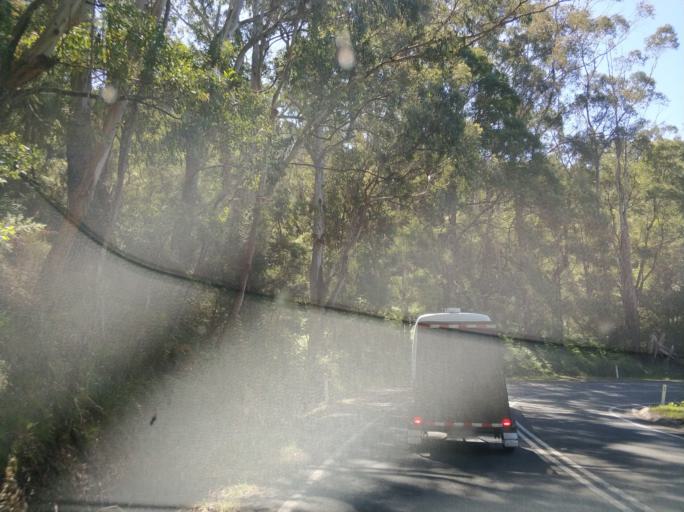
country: AU
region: Victoria
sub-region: Colac-Otway
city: Apollo Bay
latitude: -38.7360
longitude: 143.2511
